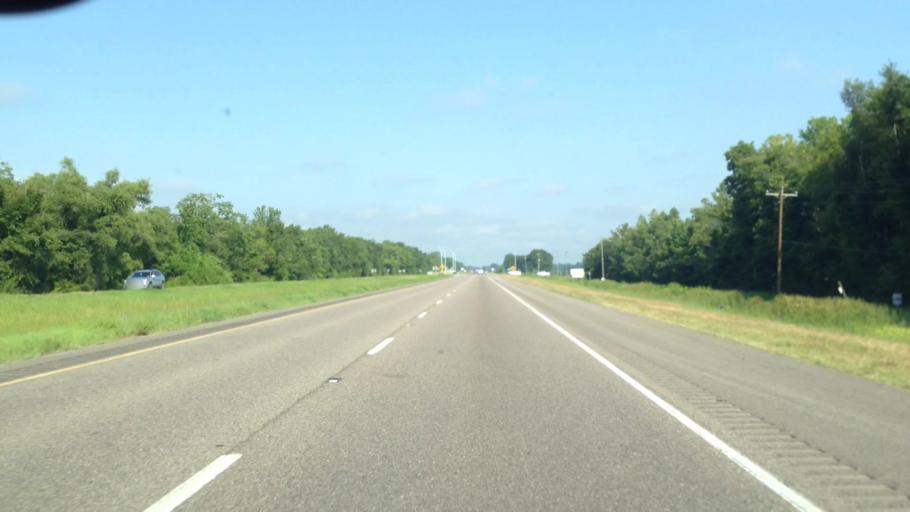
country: US
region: Louisiana
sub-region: West Baton Rouge Parish
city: Erwinville
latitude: 30.5175
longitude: -91.3605
